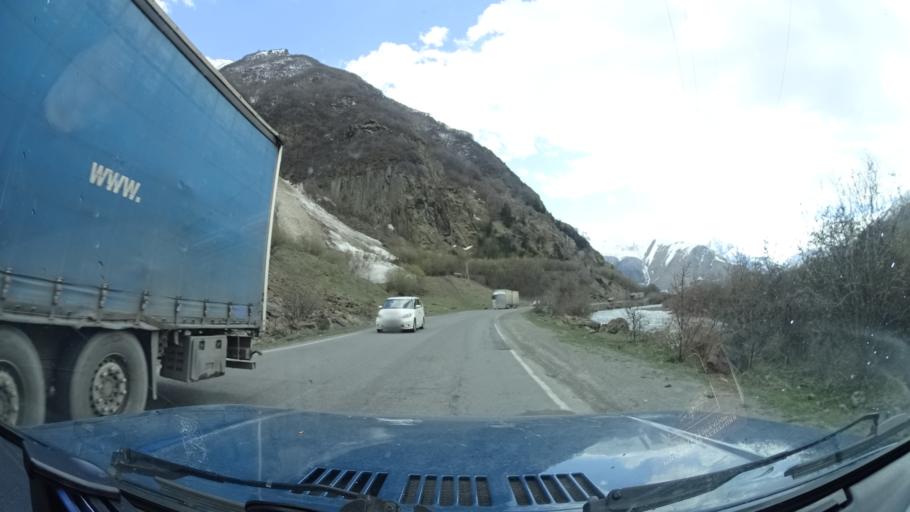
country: GE
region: Mtskheta-Mtianeti
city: Step'antsminda
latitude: 42.6401
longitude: 44.6349
